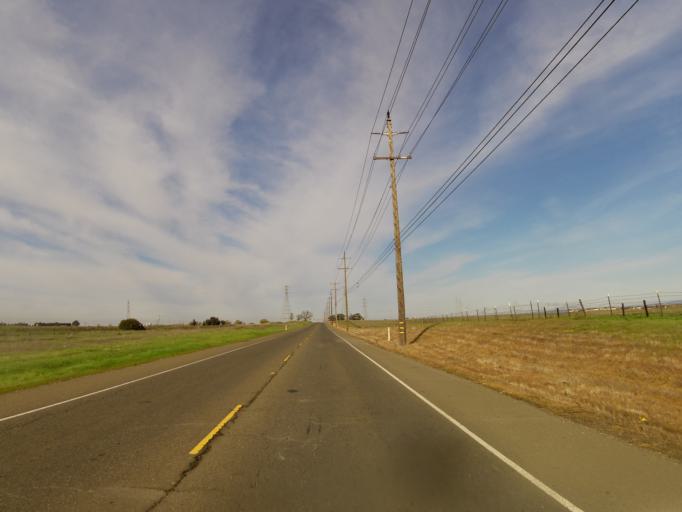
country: US
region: California
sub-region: Sacramento County
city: Rancho Cordova
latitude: 38.5168
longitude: -121.2426
